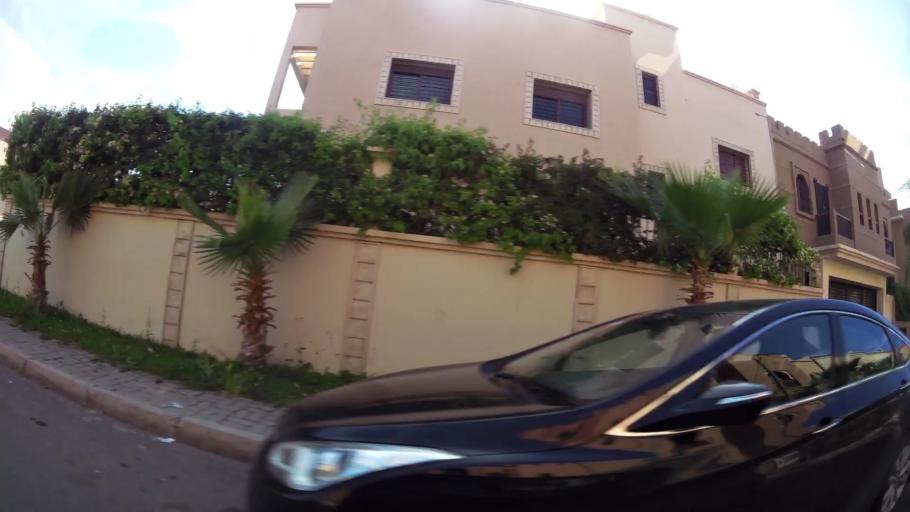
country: MA
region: Marrakech-Tensift-Al Haouz
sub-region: Marrakech
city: Marrakesh
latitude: 31.6470
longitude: -8.0436
